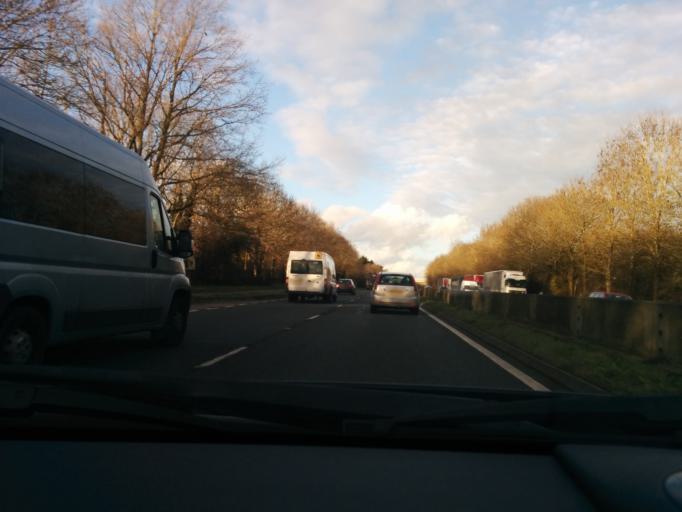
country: GB
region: England
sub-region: Oxfordshire
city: Cowley
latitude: 51.7495
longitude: -1.1954
